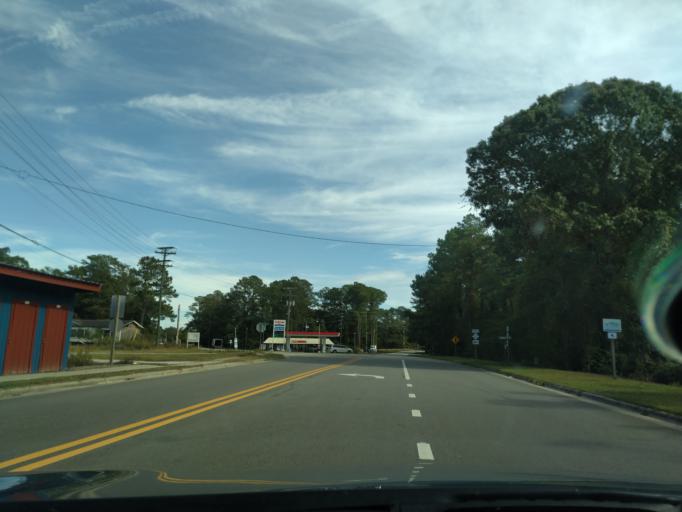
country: US
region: North Carolina
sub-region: Beaufort County
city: River Road
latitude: 35.5041
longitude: -76.9882
